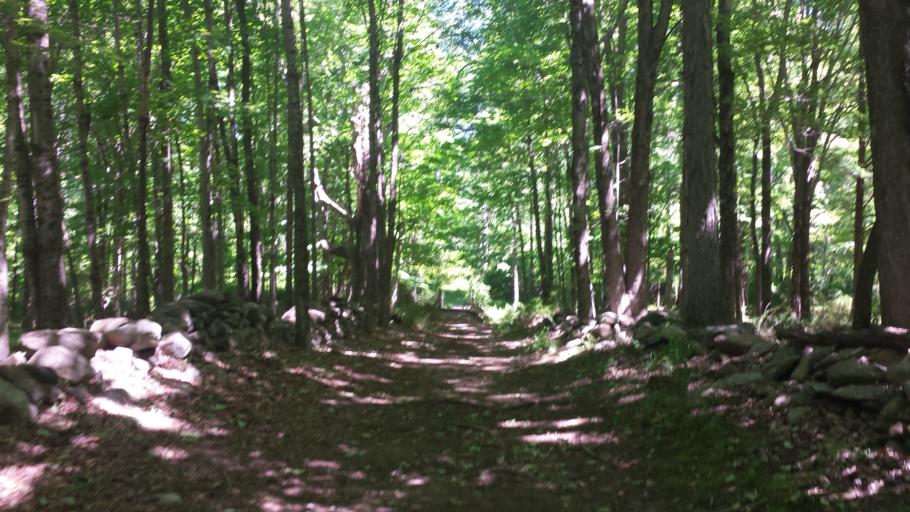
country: US
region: New York
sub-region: Westchester County
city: Pound Ridge
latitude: 41.2616
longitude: -73.5970
